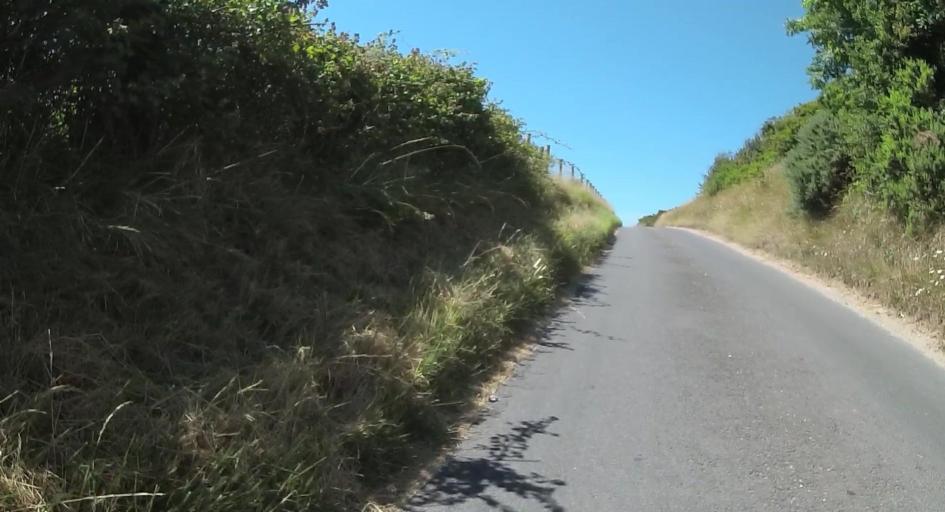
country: GB
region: England
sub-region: Dorset
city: Bovington Camp
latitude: 50.6565
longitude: -2.2988
